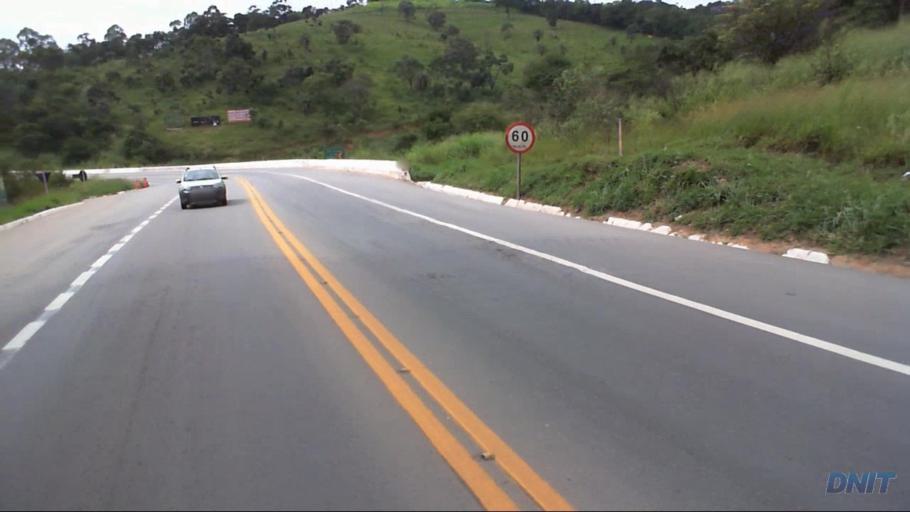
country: BR
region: Minas Gerais
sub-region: Caete
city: Caete
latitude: -19.7631
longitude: -43.6413
